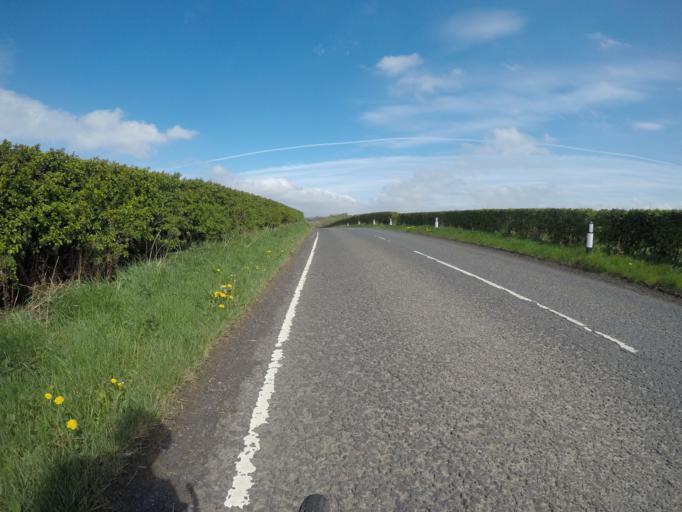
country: GB
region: Scotland
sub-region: East Ayrshire
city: Stewarton
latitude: 55.6687
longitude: -4.5327
